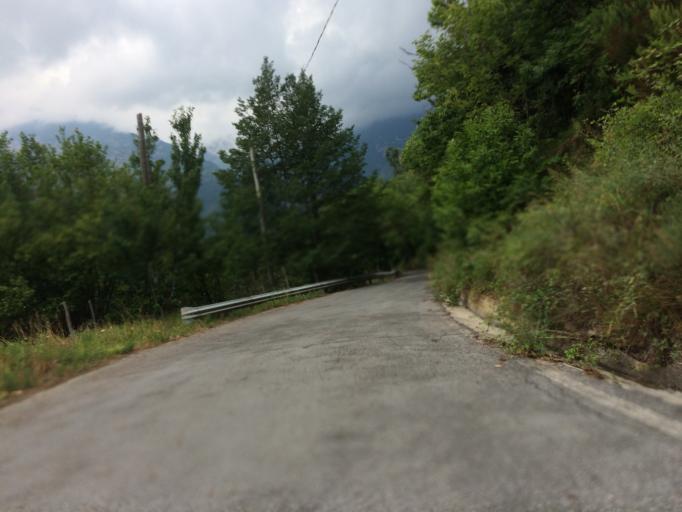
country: IT
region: Liguria
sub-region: Provincia di Imperia
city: Castel Vittorio
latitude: 43.9429
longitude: 7.6903
